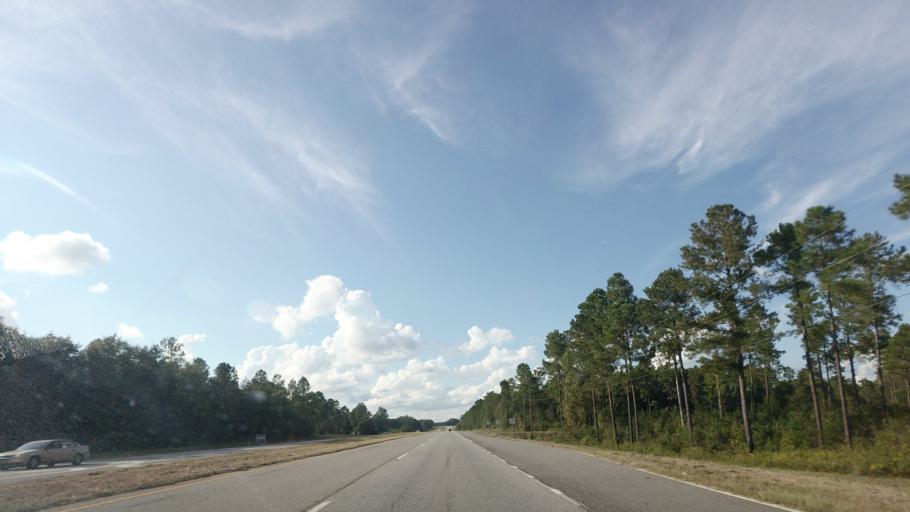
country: US
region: Georgia
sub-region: Pulaski County
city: Hawkinsville
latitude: 32.3395
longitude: -83.5678
